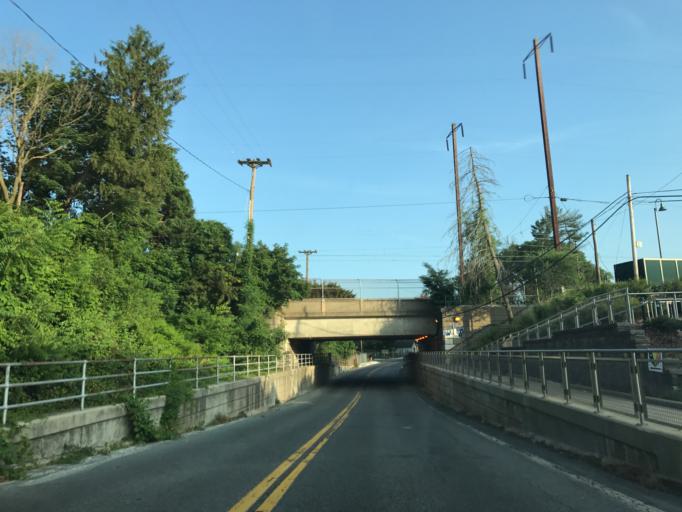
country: US
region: Maryland
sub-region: Harford County
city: Edgewood
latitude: 39.4169
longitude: -76.2924
